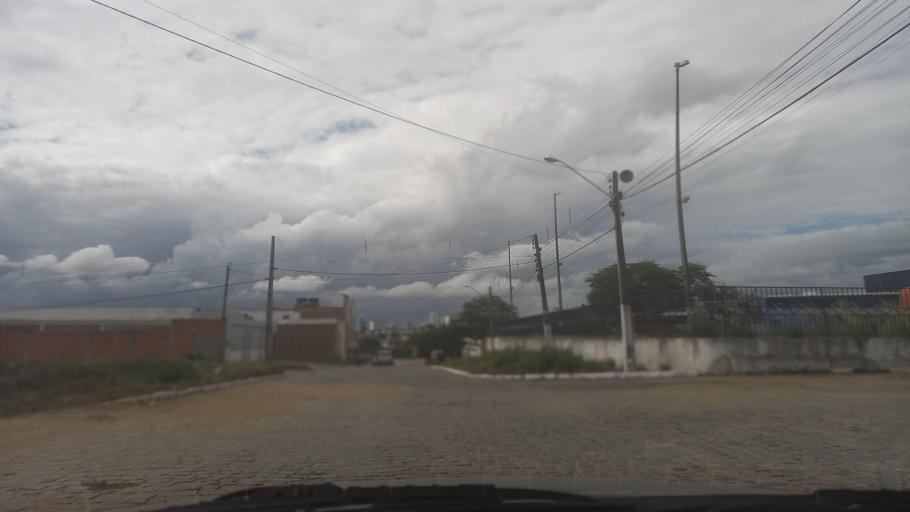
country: BR
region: Pernambuco
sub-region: Caruaru
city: Caruaru
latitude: -8.2944
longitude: -35.9892
